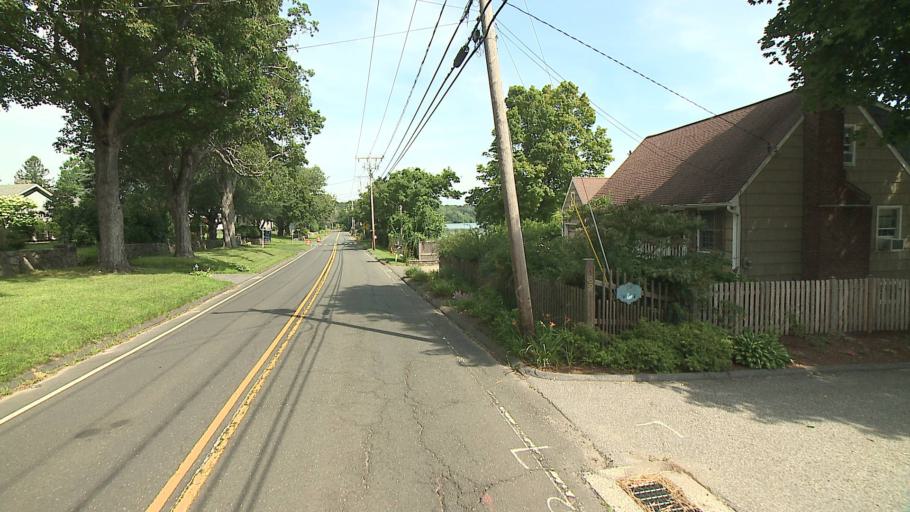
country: US
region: New York
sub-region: Putnam County
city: Putnam Lake
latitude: 41.4595
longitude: -73.5249
